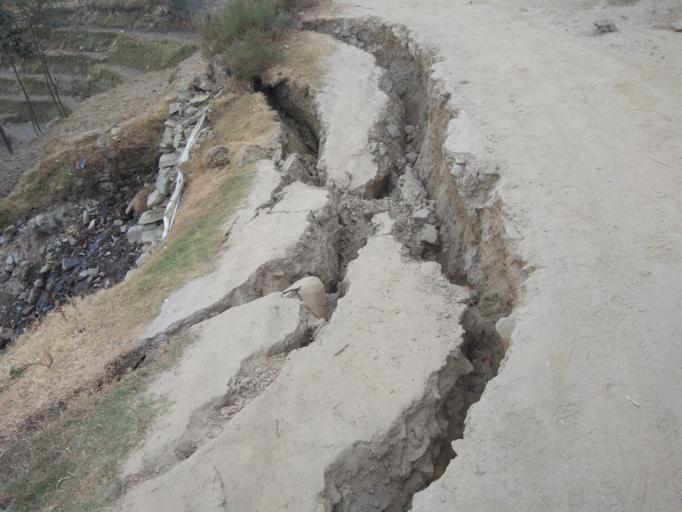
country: NP
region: Far Western
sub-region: Seti Zone
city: Achham
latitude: 29.2571
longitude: 81.6306
